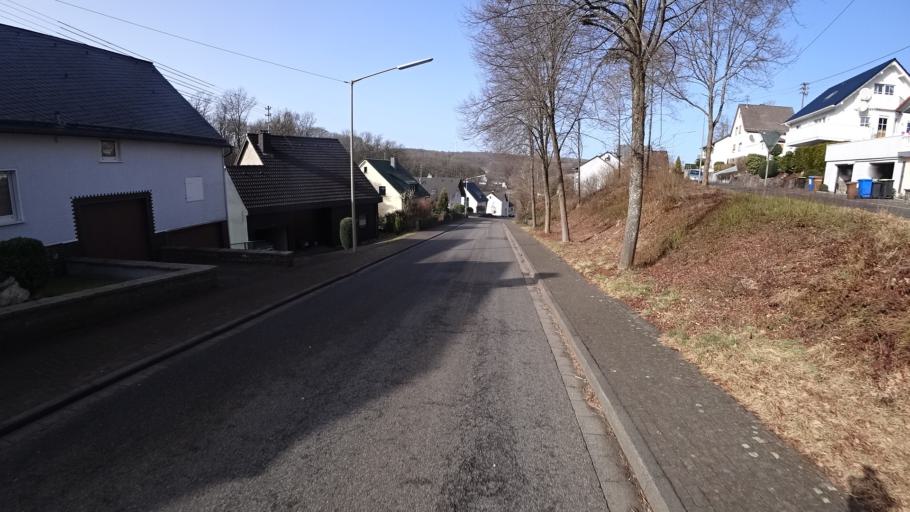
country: DE
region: Rheinland-Pfalz
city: Dickendorf
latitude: 50.7319
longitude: 7.8337
